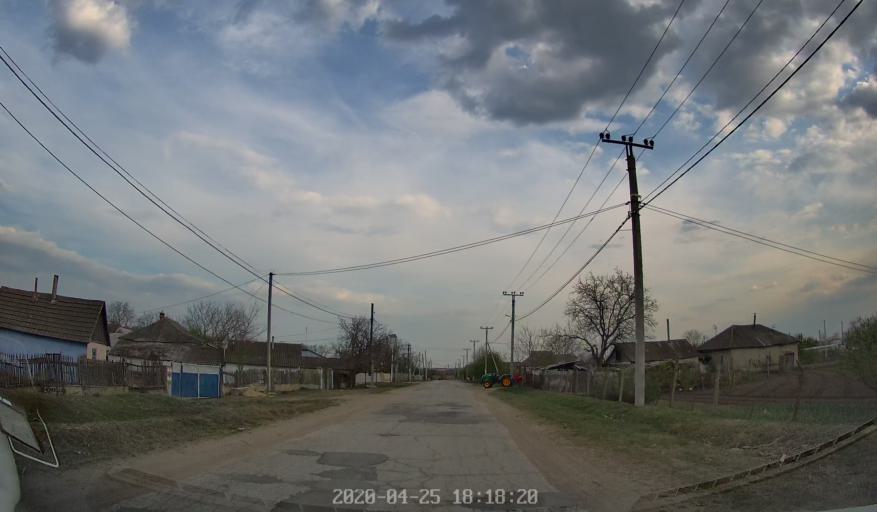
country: MD
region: Criuleni
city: Criuleni
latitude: 47.1646
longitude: 29.1276
